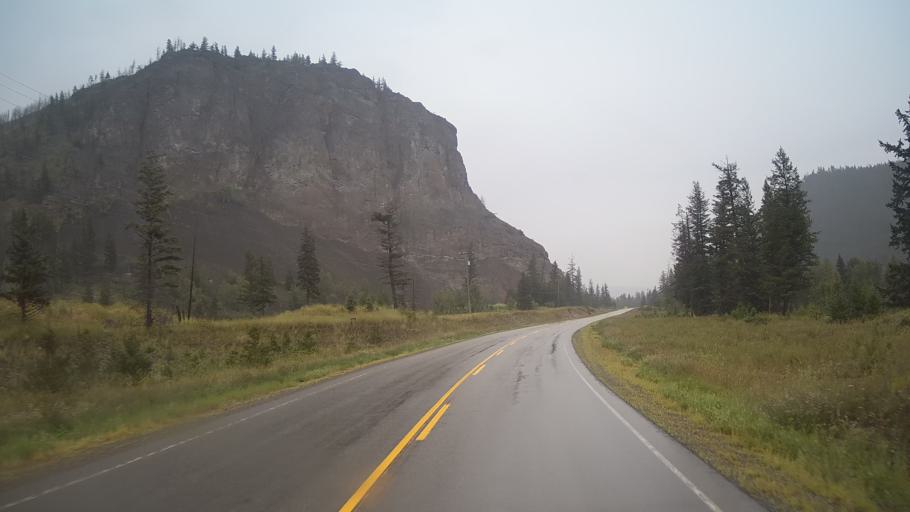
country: CA
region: British Columbia
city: Hanceville
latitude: 52.0875
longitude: -123.3690
